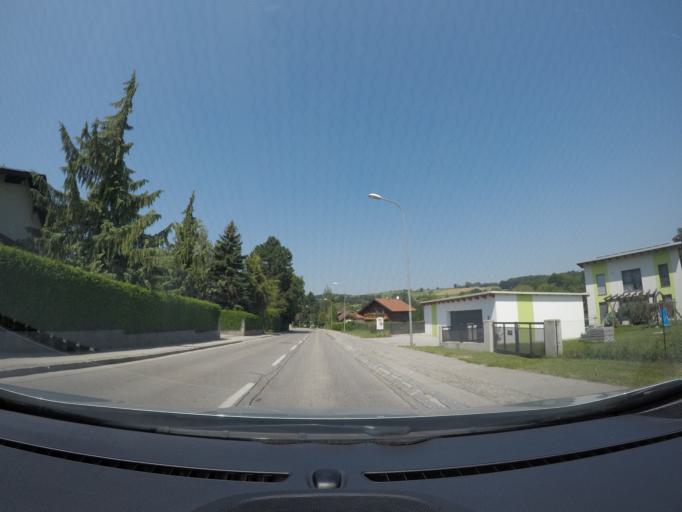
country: AT
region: Lower Austria
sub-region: Politischer Bezirk Sankt Polten
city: Eichgraben
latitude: 48.1835
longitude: 15.9660
